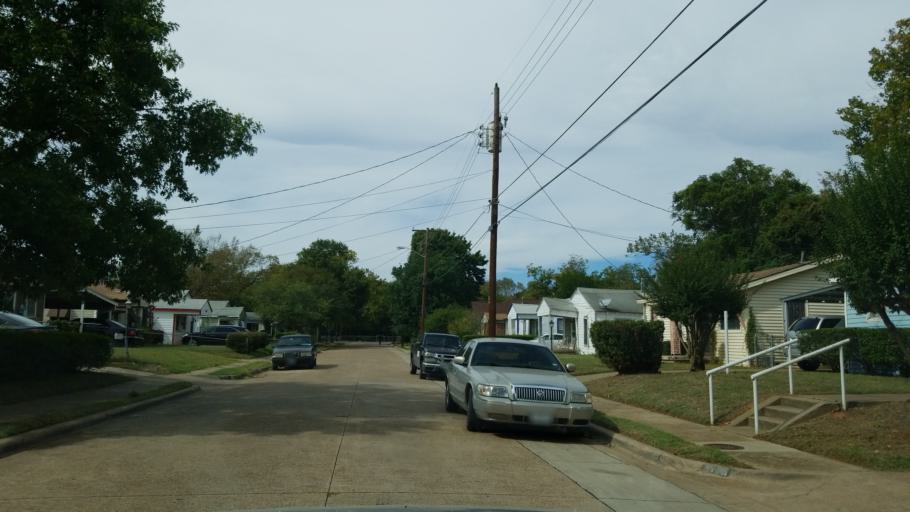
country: US
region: Texas
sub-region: Dallas County
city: Dallas
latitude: 32.7637
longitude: -96.7362
